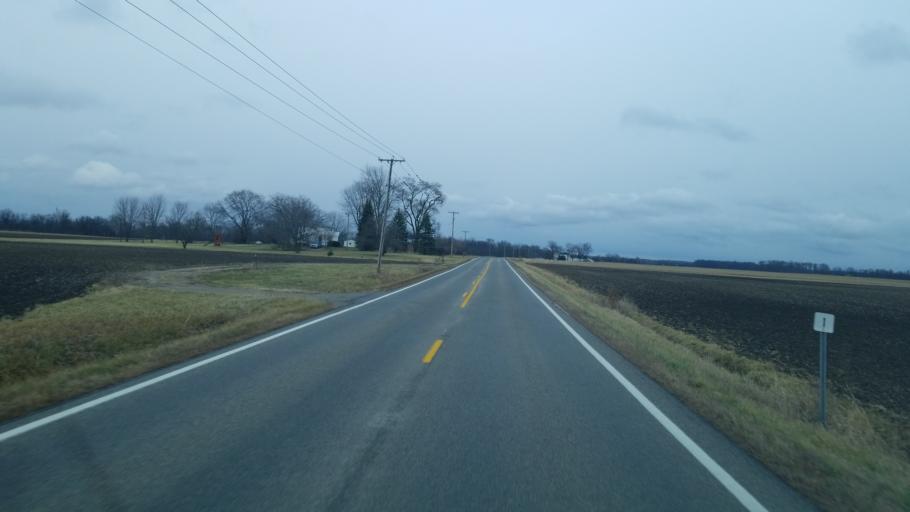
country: US
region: Ohio
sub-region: Union County
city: Richwood
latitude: 40.3374
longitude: -83.2310
